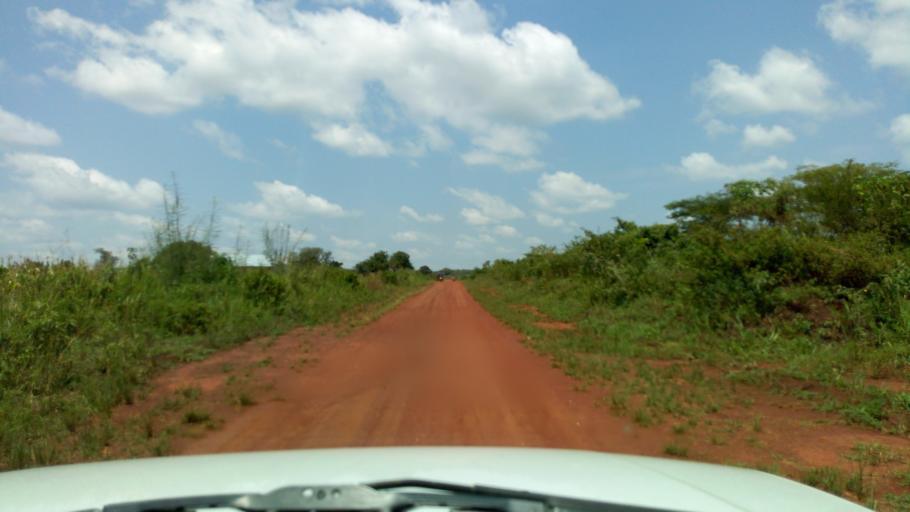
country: UG
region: Western Region
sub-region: Masindi District
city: Masindi
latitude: 1.7340
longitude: 31.8815
